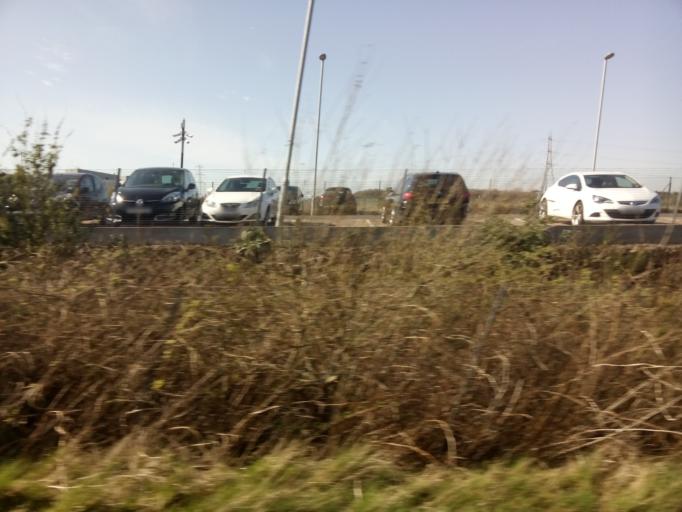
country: GB
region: Scotland
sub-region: East Lothian
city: Musselburgh
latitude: 55.9341
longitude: -3.0744
